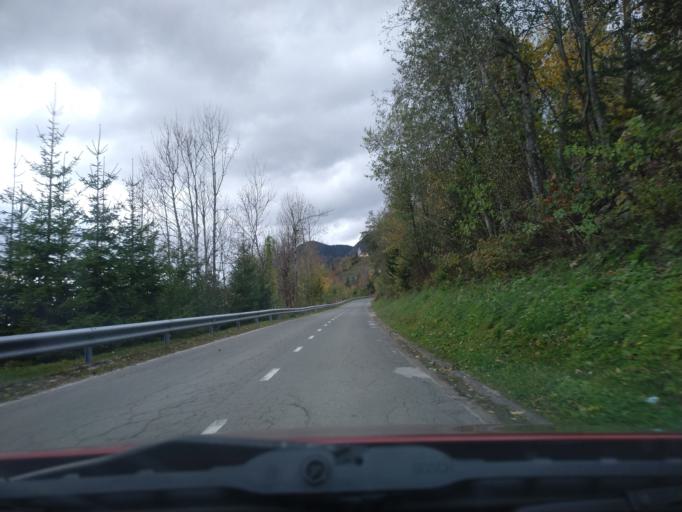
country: SI
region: Kamnik
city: Mekinje
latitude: 46.2594
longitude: 14.6923
